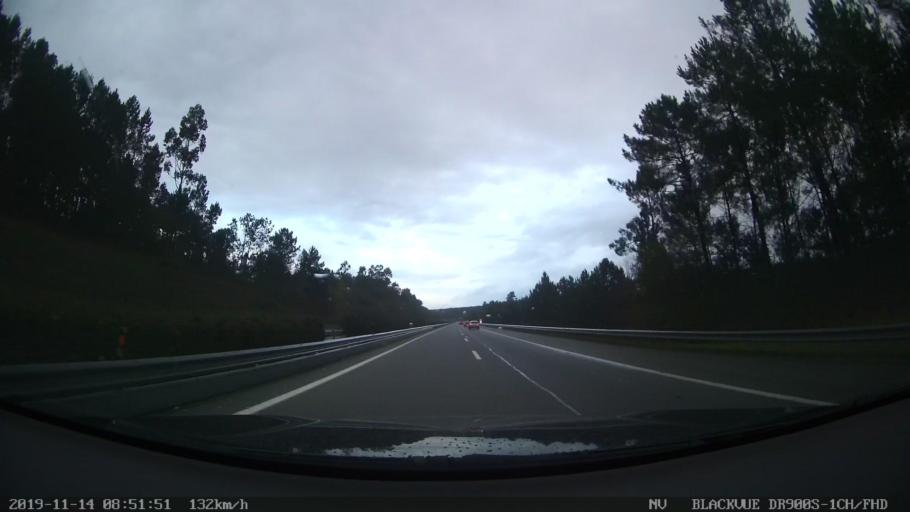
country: PT
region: Viana do Castelo
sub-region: Vila Nova de Cerveira
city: Vila Nova de Cerveira
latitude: 41.9166
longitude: -8.6567
